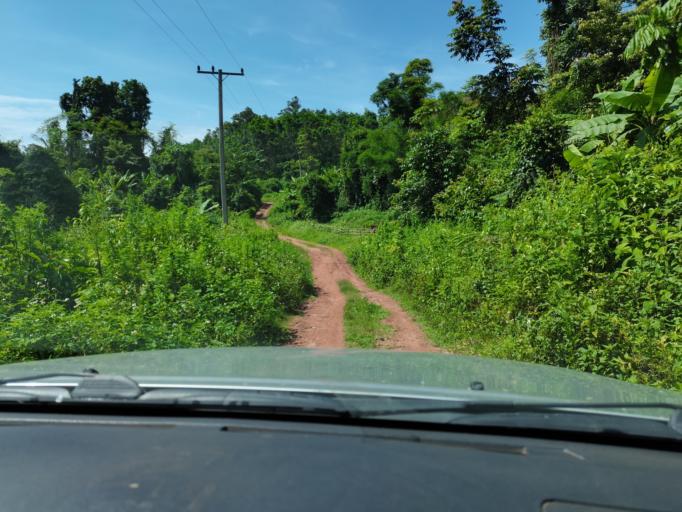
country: LA
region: Loungnamtha
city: Muang Nale
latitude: 20.5320
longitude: 101.0648
